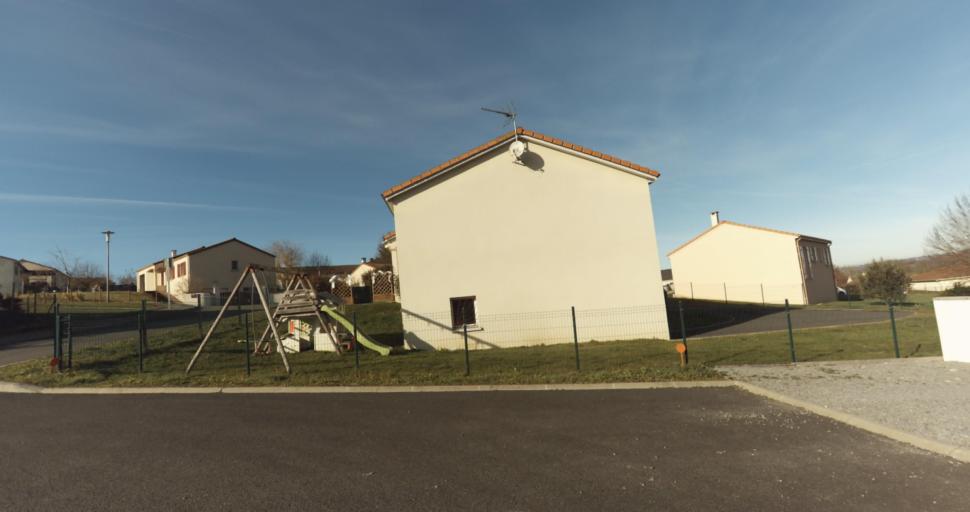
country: FR
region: Limousin
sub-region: Departement de la Haute-Vienne
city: Aixe-sur-Vienne
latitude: 45.7905
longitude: 1.1265
